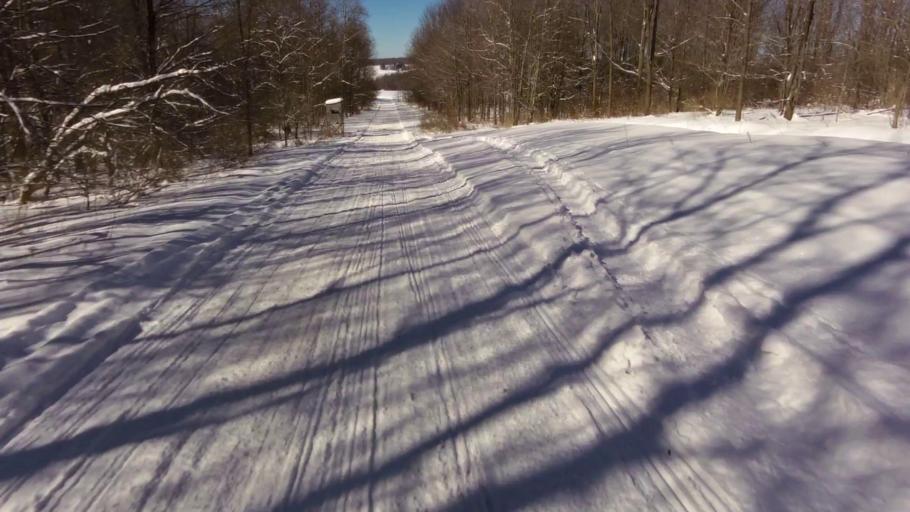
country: US
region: New York
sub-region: Chautauqua County
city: Mayville
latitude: 42.2468
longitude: -79.4218
